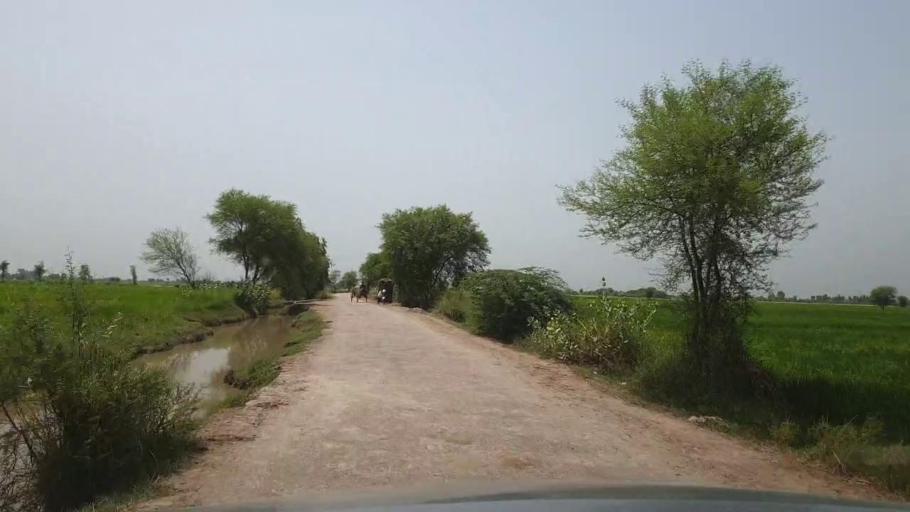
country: PK
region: Sindh
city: Madeji
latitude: 27.7802
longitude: 68.4322
